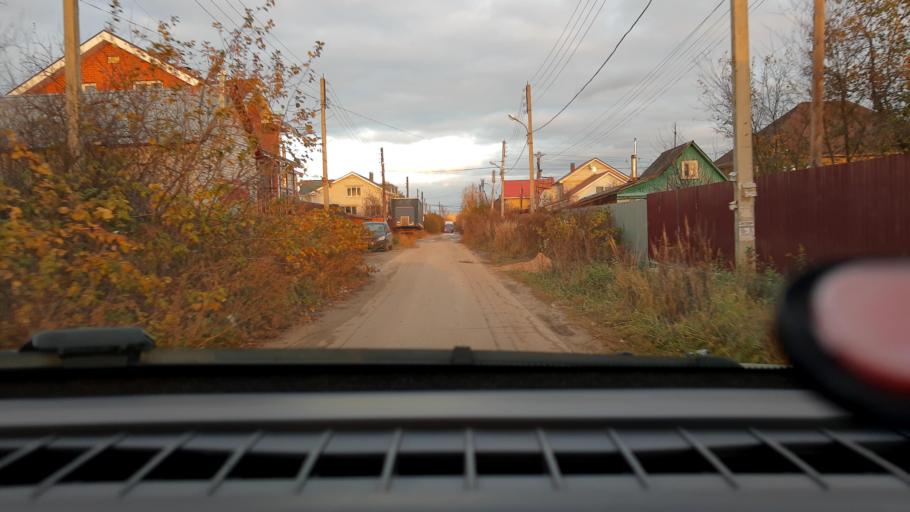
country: RU
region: Nizjnij Novgorod
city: Gorbatovka
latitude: 56.2959
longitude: 43.8478
